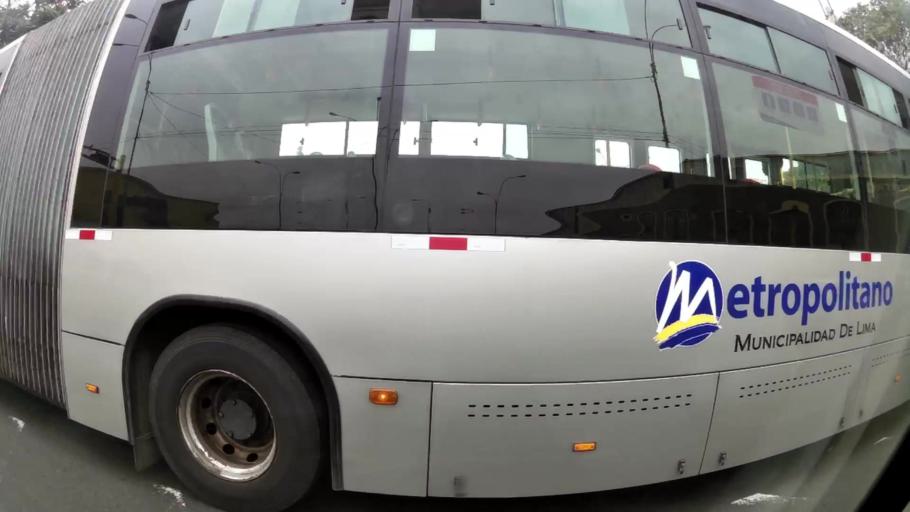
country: PE
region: Lima
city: Lima
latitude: -12.0429
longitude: -77.0432
